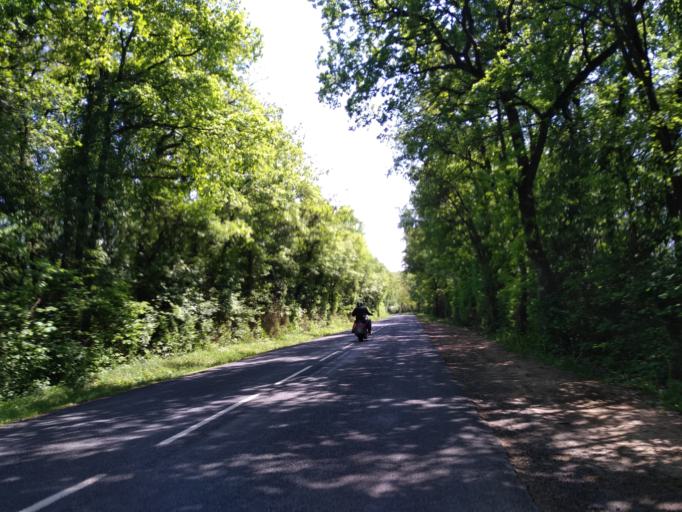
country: FR
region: Rhone-Alpes
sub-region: Departement du Rhone
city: Limonest
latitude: 45.8369
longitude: 4.7991
